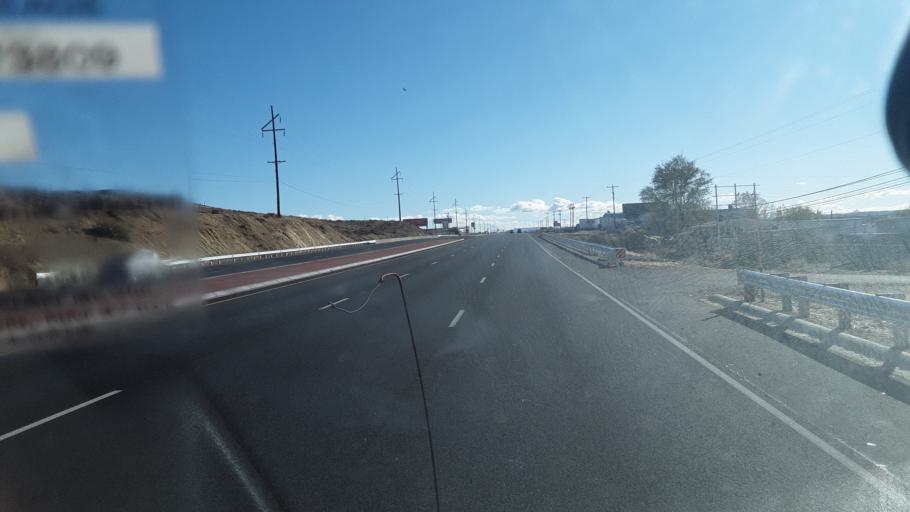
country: US
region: New Mexico
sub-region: San Juan County
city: Lee Acres
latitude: 36.7064
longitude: -108.1198
